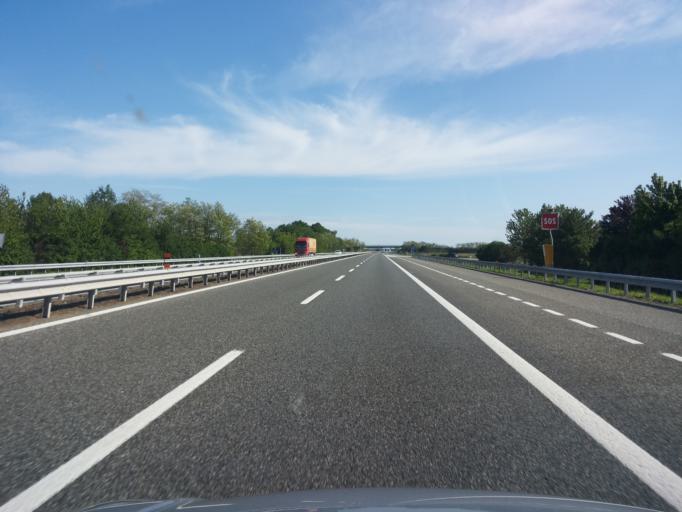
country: IT
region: Piedmont
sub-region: Provincia di Novara
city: Landiona
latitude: 45.5029
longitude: 8.4362
